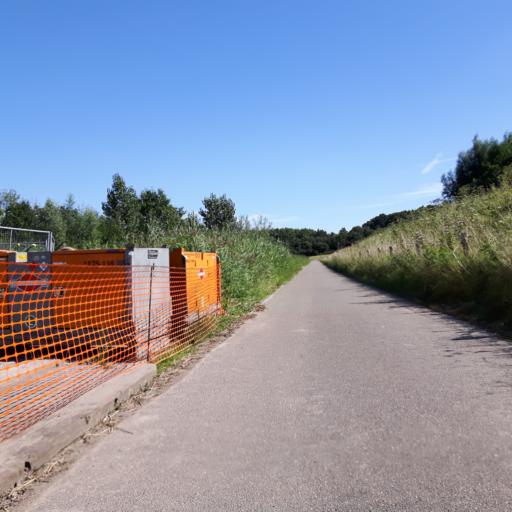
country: NL
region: North Brabant
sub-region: Gemeente Bergen op Zoom
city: Bergen op Zoom
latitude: 51.4711
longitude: 4.2890
